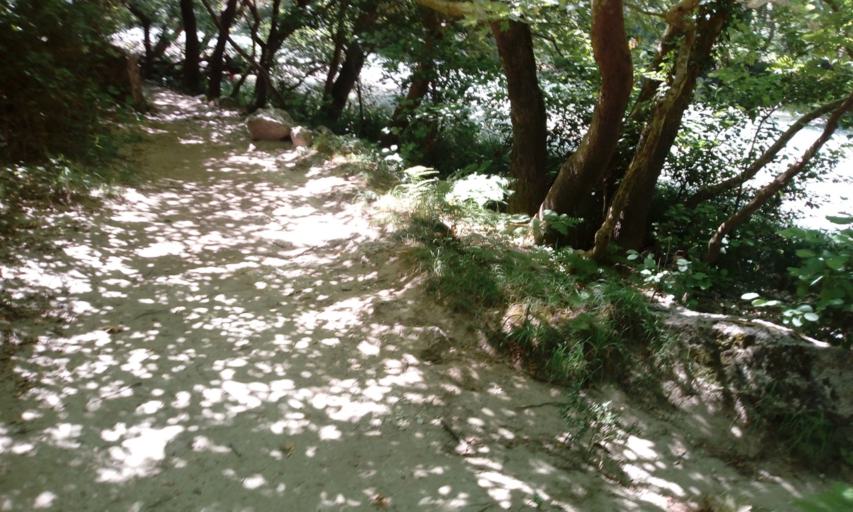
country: GR
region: Epirus
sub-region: Nomos Prevezis
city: Kanalaki
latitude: 39.3274
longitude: 20.6244
